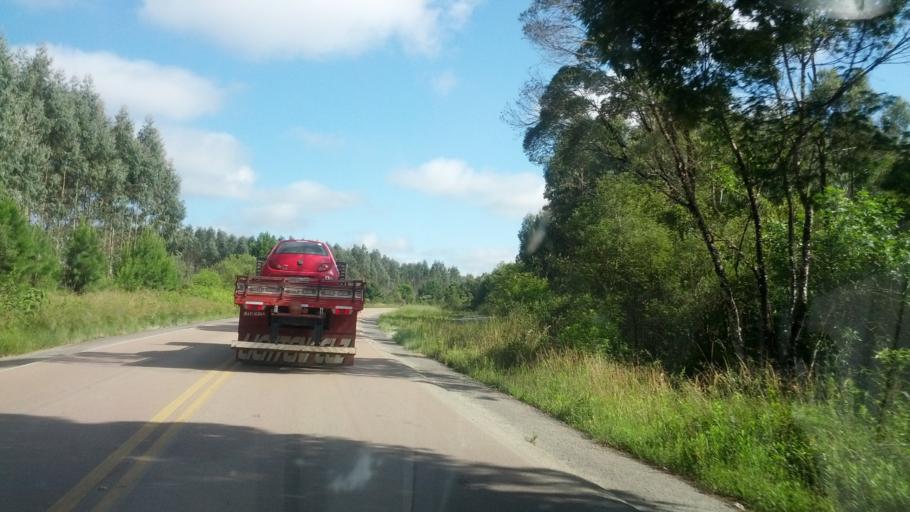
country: BR
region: Santa Catarina
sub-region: Otacilio Costa
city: Otacilio Costa
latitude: -27.4440
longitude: -50.1254
